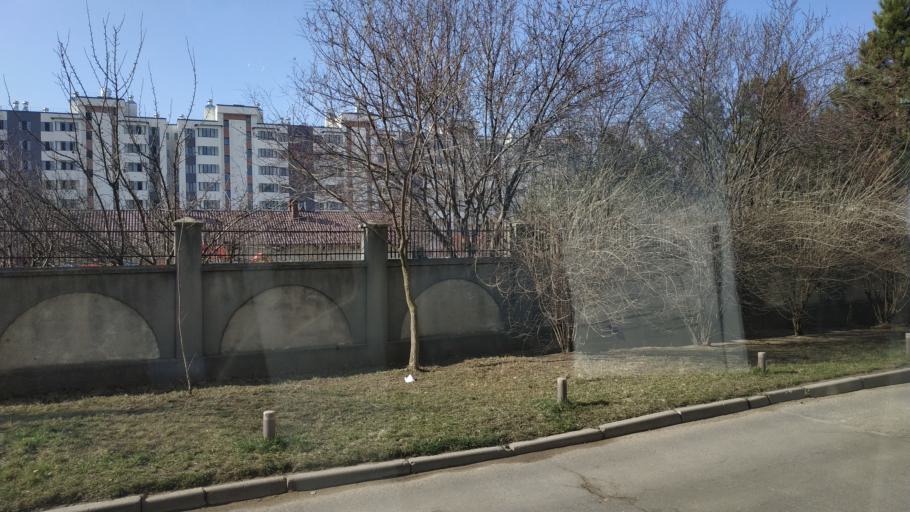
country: MD
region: Chisinau
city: Vatra
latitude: 47.0394
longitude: 28.7641
